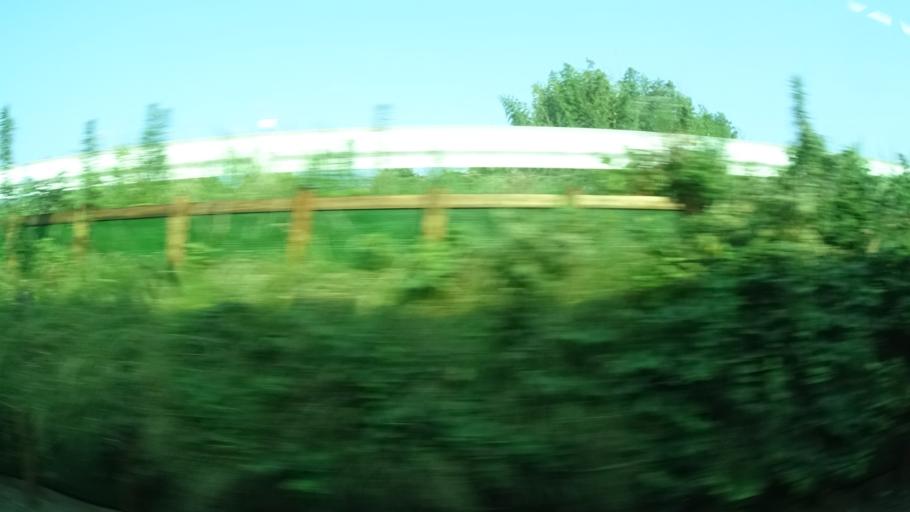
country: JP
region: Ibaraki
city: Takahagi
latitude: 36.6769
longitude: 140.6901
